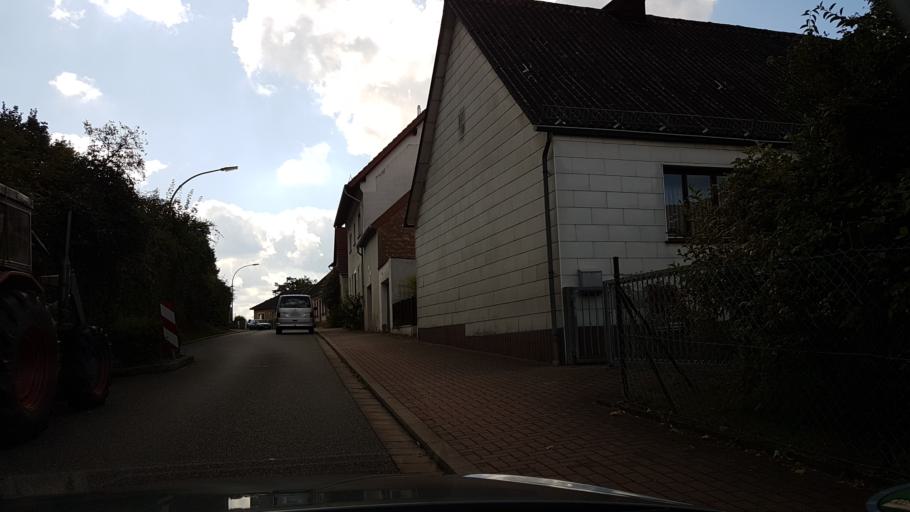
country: DE
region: Saarland
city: Bexbach
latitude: 49.3201
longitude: 7.2857
